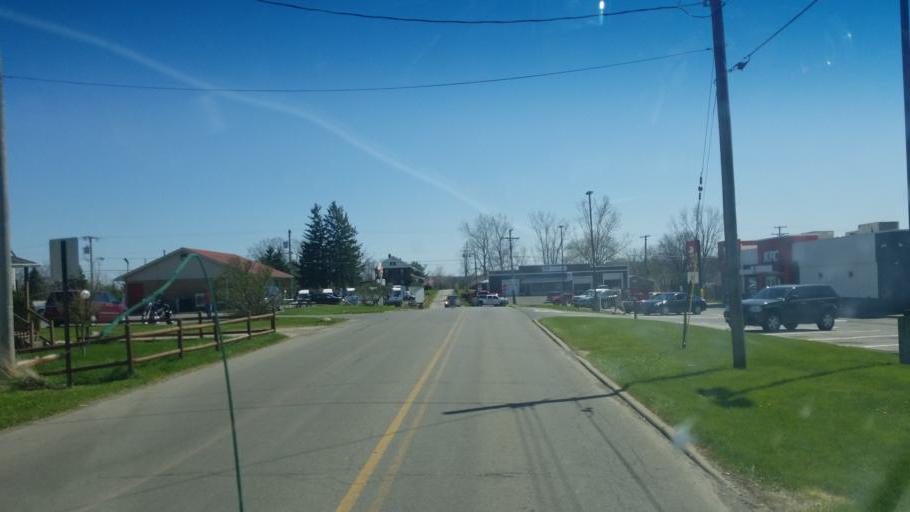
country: US
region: Ohio
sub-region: Richland County
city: Lincoln Heights
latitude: 40.7641
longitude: -82.4970
